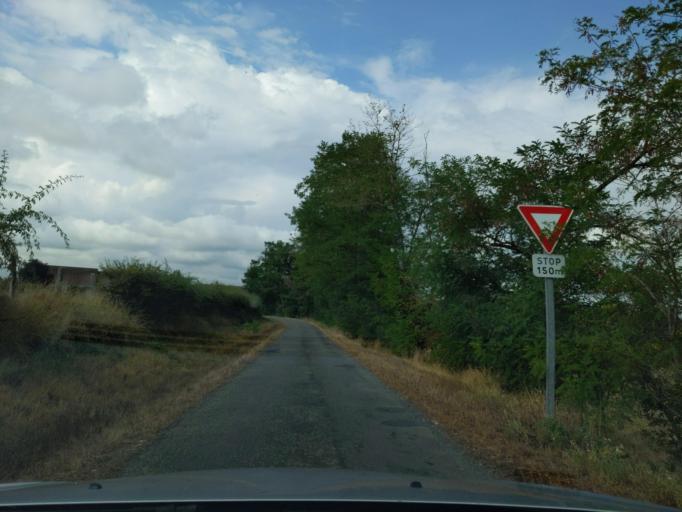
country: FR
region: Bourgogne
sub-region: Departement de Saone-et-Loire
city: Bourbon-Lancy
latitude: 46.6331
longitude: 3.7258
